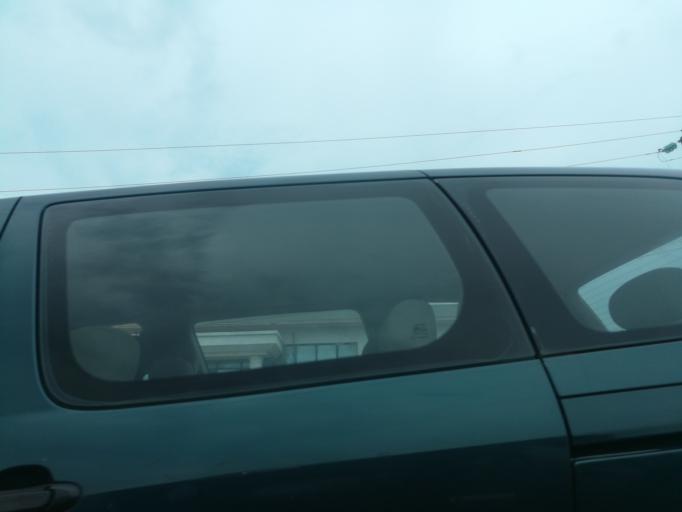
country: NG
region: Oyo
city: Ibadan
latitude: 7.3904
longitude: 3.9559
